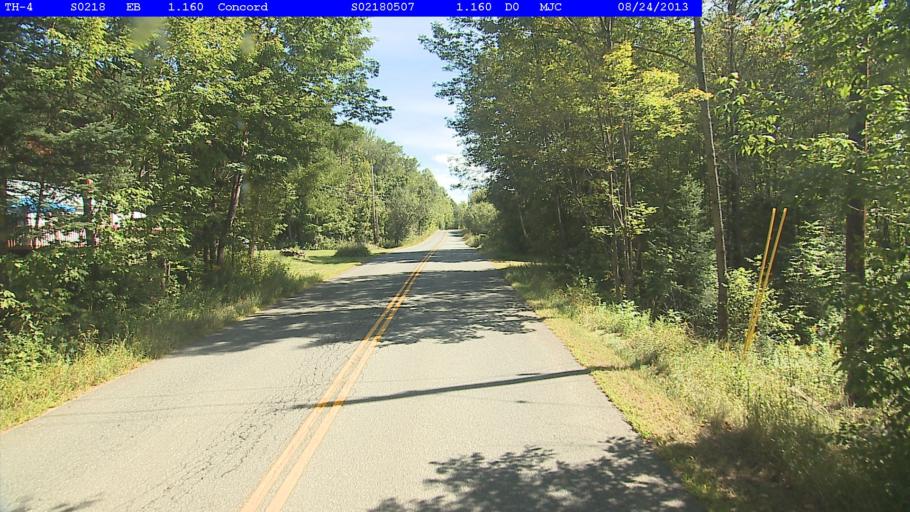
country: US
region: New Hampshire
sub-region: Grafton County
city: Littleton
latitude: 44.4494
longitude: -71.7673
